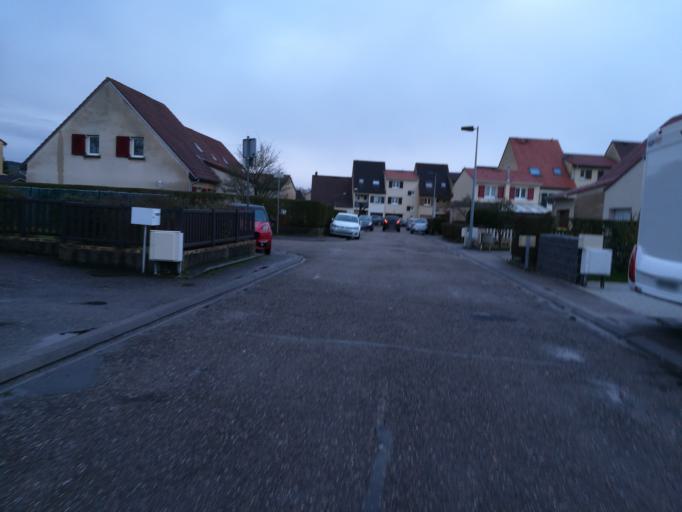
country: FR
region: Lorraine
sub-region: Departement de la Moselle
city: Ars-sur-Moselle
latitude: 49.0741
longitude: 6.0755
